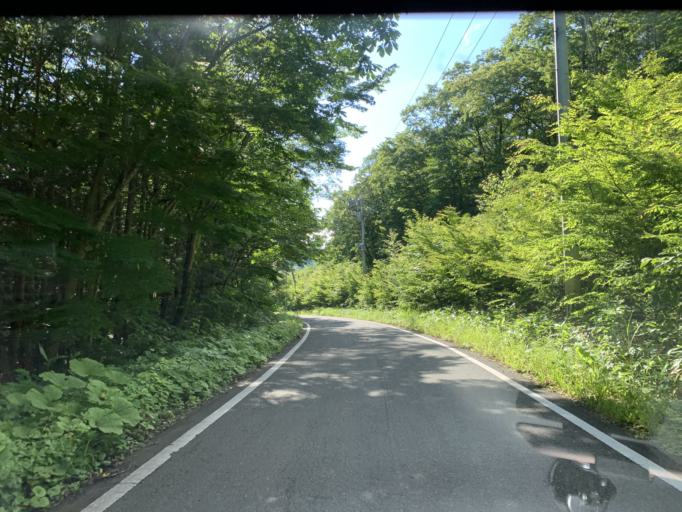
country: JP
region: Iwate
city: Ichinoseki
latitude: 38.9031
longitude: 140.8571
